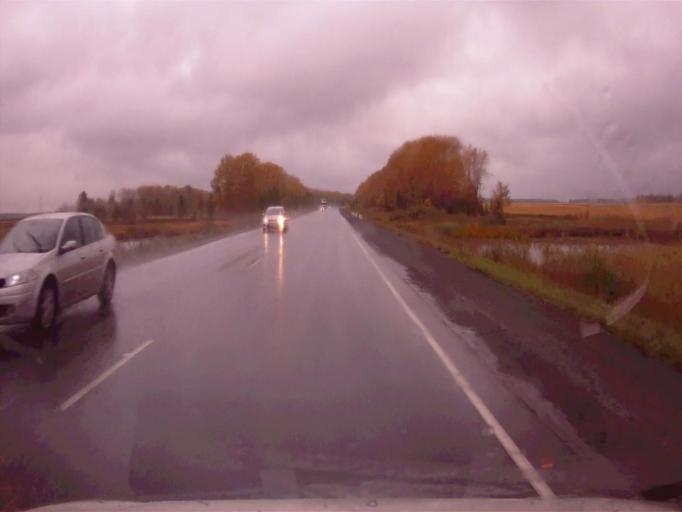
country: RU
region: Chelyabinsk
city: Argayash
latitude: 55.4473
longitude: 60.9463
